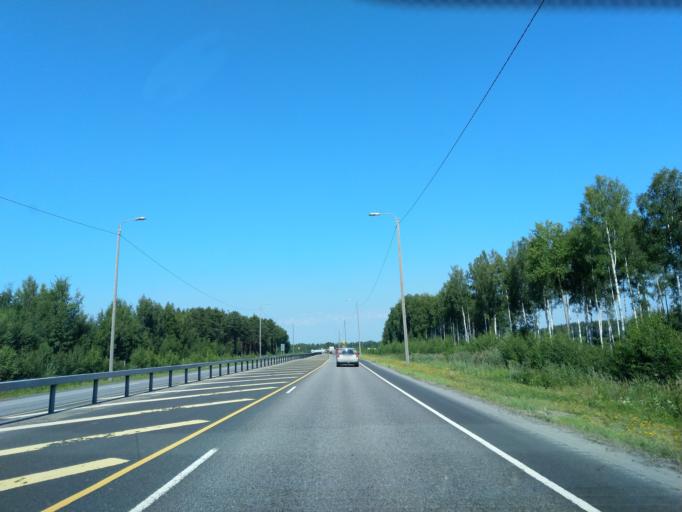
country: FI
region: Satakunta
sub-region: Pori
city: Nakkila
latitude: 61.3440
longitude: 22.0274
